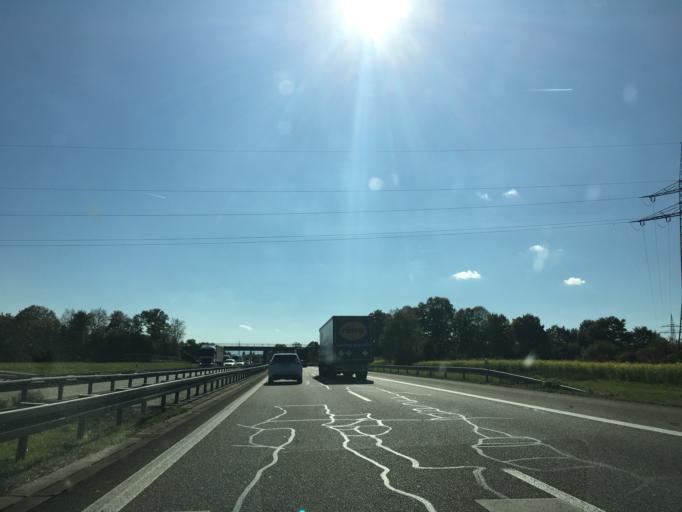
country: FR
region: Alsace
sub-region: Departement du Haut-Rhin
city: Kembs
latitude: 47.6987
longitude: 7.5211
